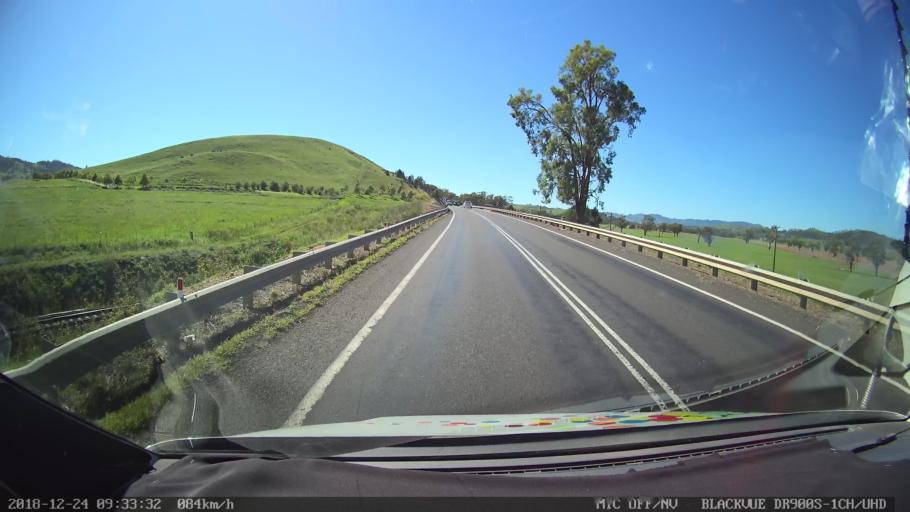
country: AU
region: New South Wales
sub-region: Liverpool Plains
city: Quirindi
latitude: -31.6046
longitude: 150.7084
